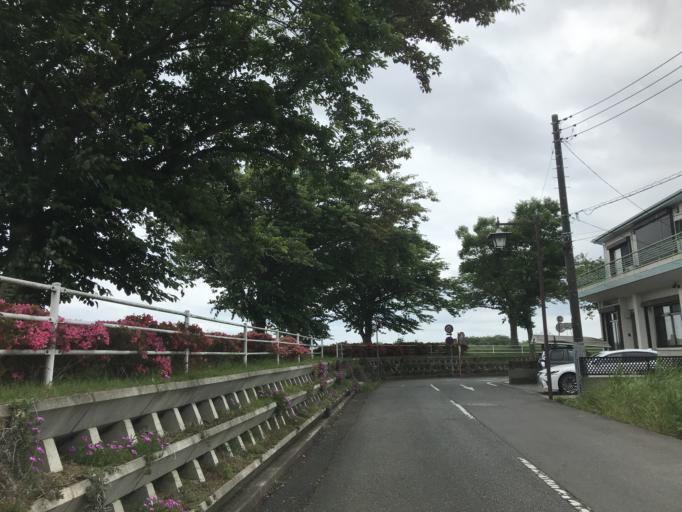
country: JP
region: Ibaraki
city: Ami
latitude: 36.0771
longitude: 140.2187
